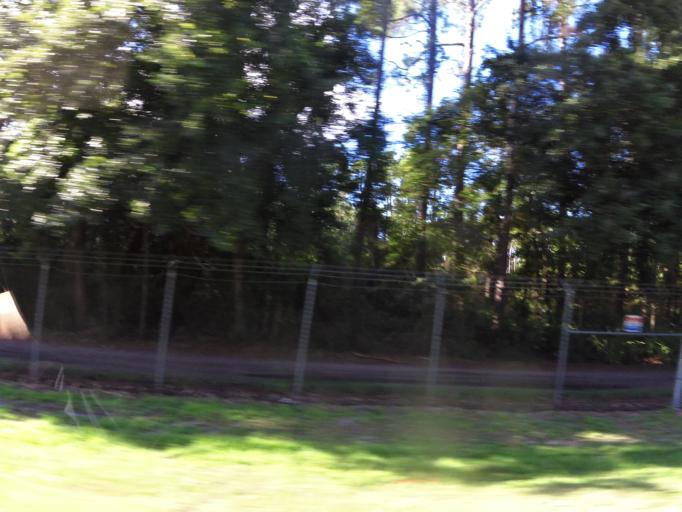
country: US
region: Georgia
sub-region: Glynn County
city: Country Club Estates
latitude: 31.2269
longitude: -81.4676
